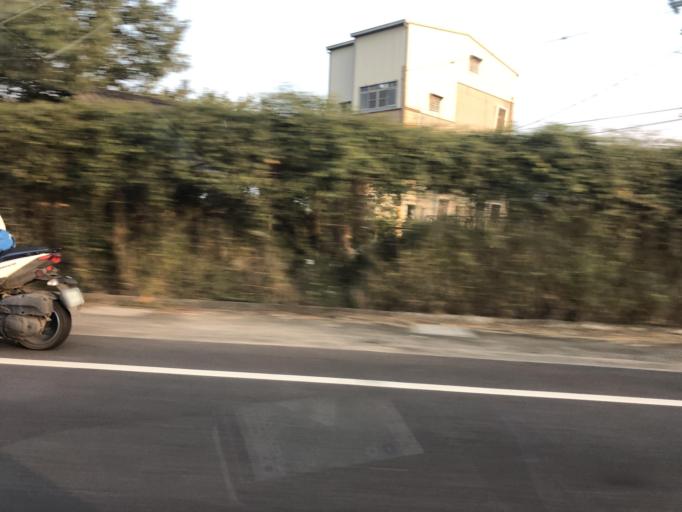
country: TW
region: Taiwan
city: Xinying
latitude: 23.2018
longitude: 120.2693
